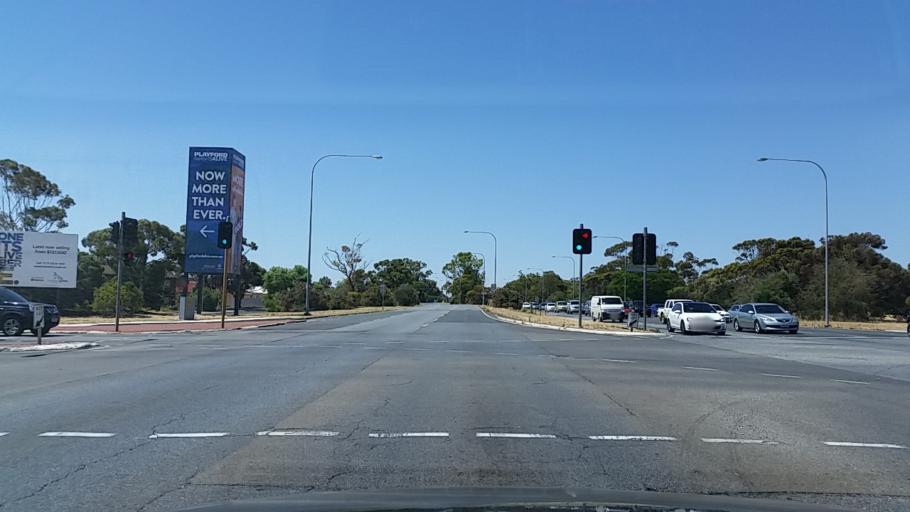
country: AU
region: South Australia
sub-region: Salisbury
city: Elizabeth
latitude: -34.7074
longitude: 138.6784
